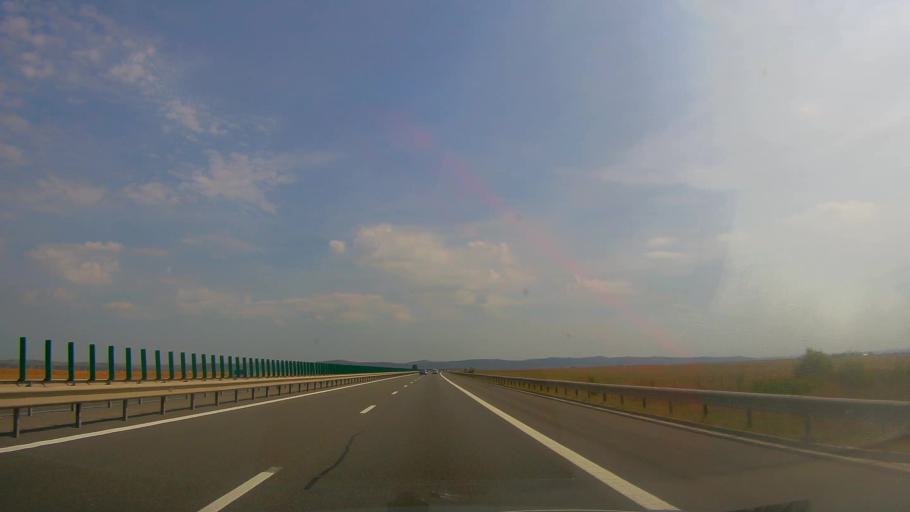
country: RO
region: Cluj
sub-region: Municipiul Campia Turzii
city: Campia Turzii
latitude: 46.5260
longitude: 23.8386
